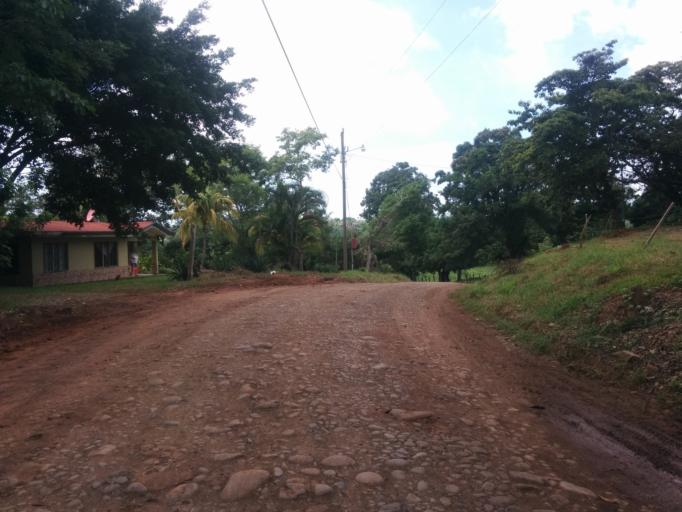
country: CR
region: Puntarenas
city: Esparza
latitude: 10.0166
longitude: -84.6888
